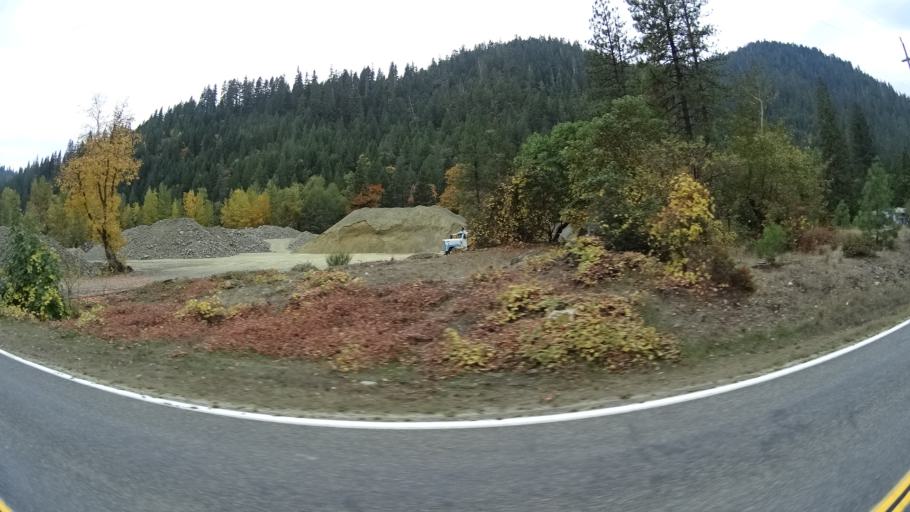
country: US
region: California
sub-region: Siskiyou County
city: Happy Camp
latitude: 41.8858
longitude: -123.4322
